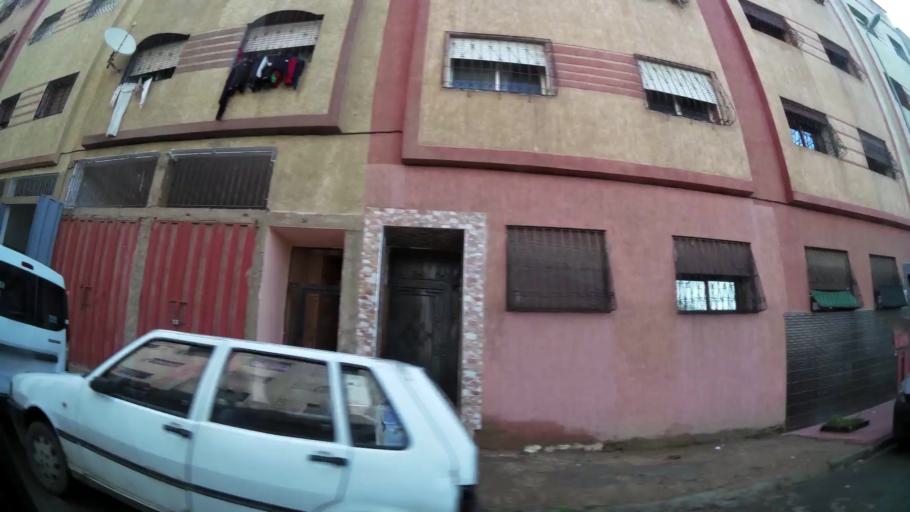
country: MA
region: Grand Casablanca
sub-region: Mediouna
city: Tit Mellil
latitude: 33.5921
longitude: -7.5214
